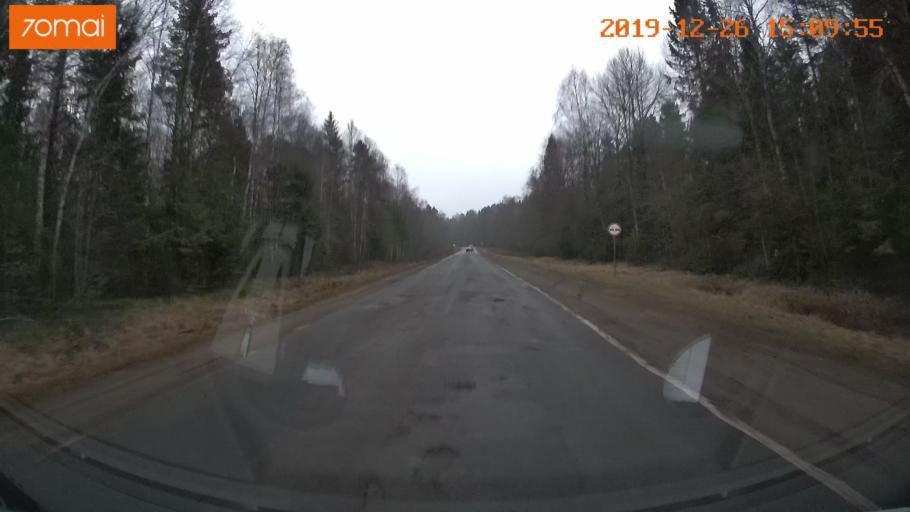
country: RU
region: Jaroslavl
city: Rybinsk
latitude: 58.1448
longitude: 38.8457
